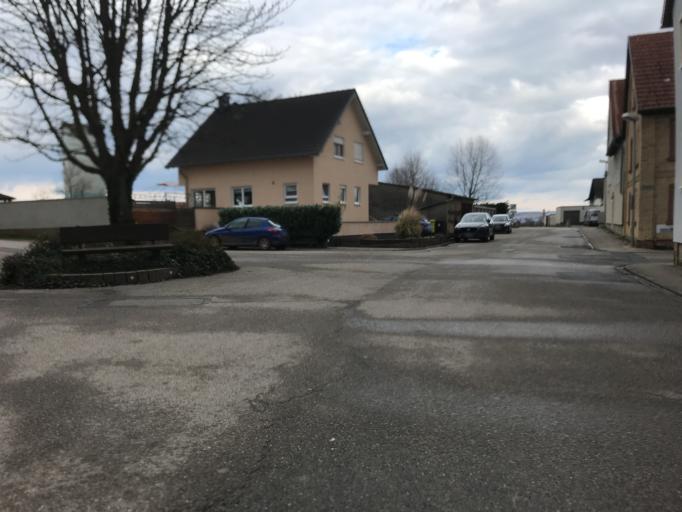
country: DE
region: Rheinland-Pfalz
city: Ober-Saulheim
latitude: 49.8794
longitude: 8.1529
